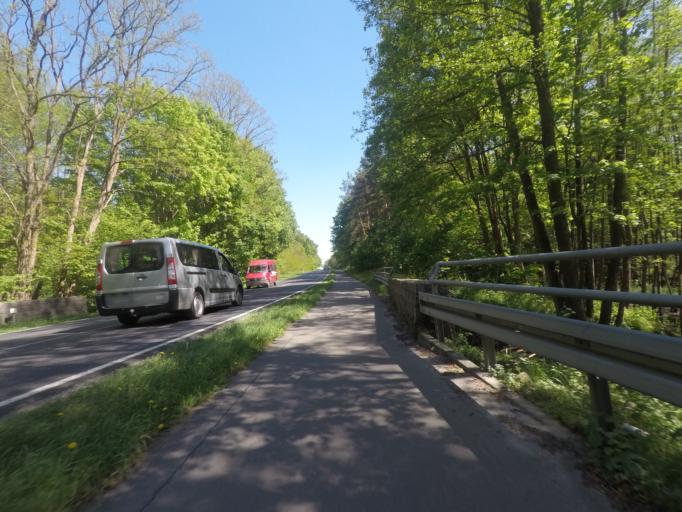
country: DE
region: Brandenburg
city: Melchow
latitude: 52.8403
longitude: 13.7073
